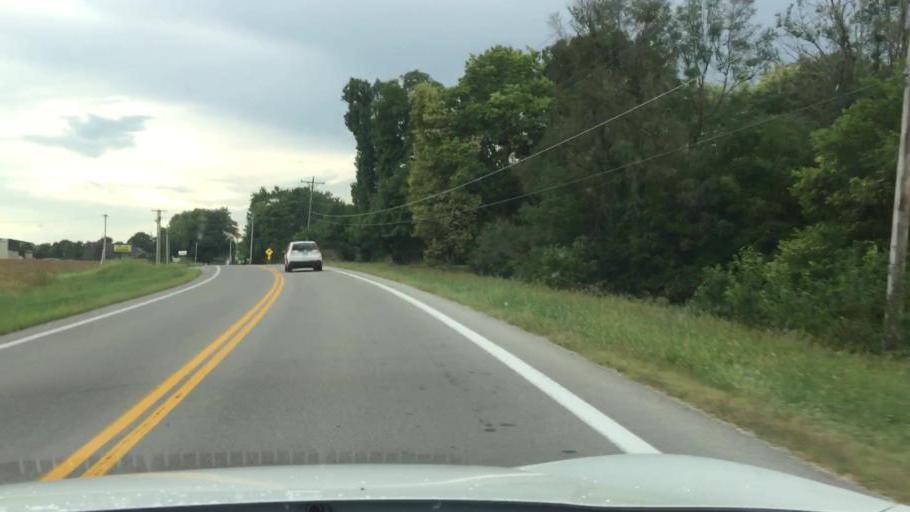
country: US
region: Ohio
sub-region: Champaign County
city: North Lewisburg
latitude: 40.2224
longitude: -83.5465
